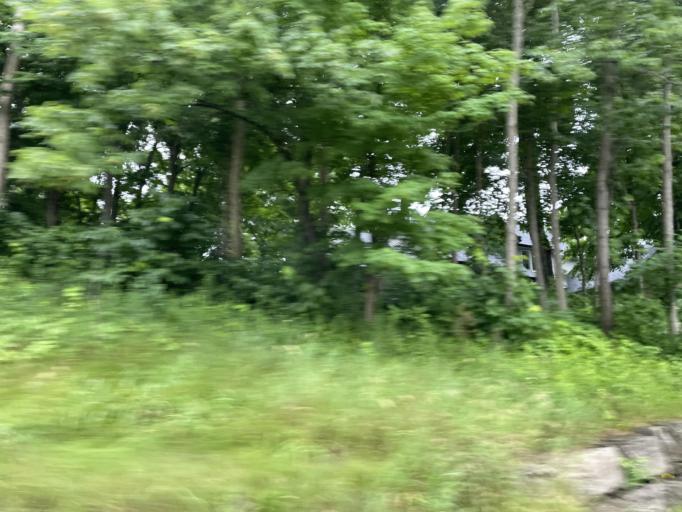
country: CA
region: Ontario
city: Cambridge
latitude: 43.4437
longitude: -80.2615
